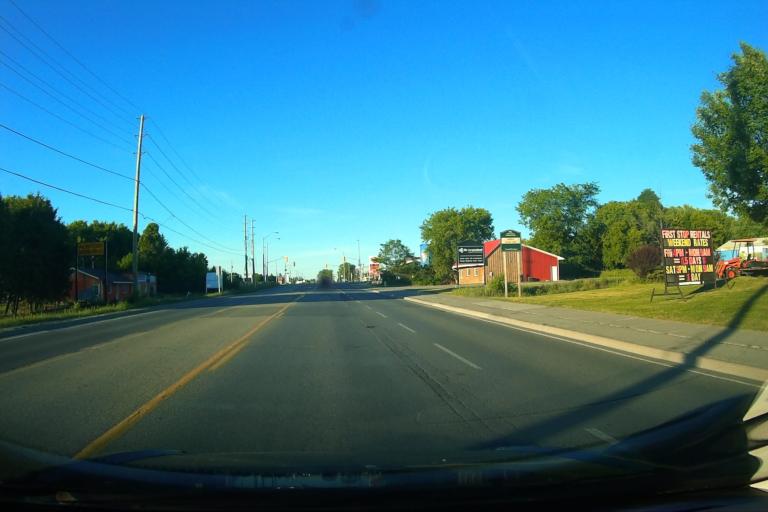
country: CA
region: Ontario
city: Prescott
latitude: 45.0205
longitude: -75.6544
